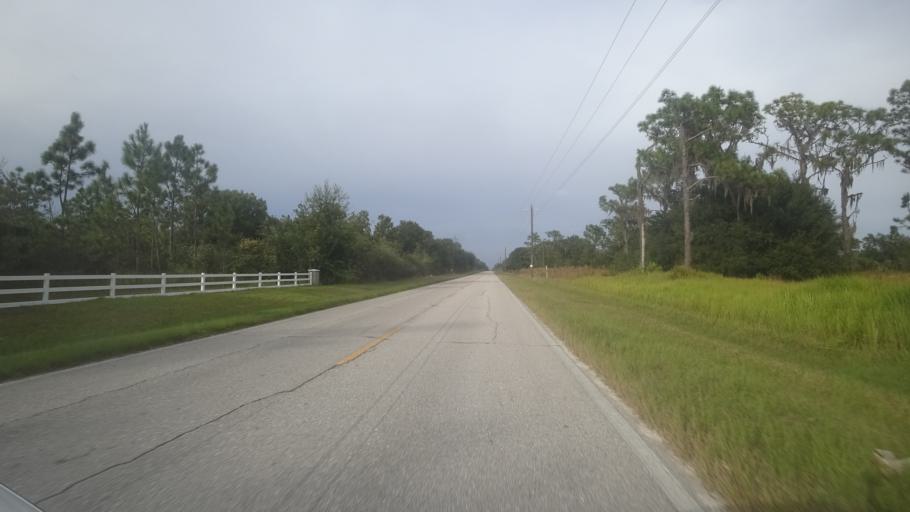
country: US
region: Florida
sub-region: Sarasota County
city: The Meadows
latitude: 27.4195
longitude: -82.2709
